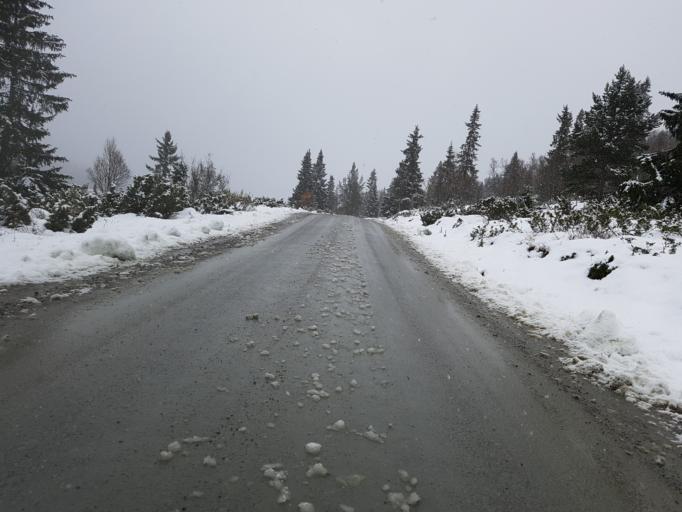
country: NO
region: Oppland
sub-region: Sel
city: Otta
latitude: 61.7940
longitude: 9.7159
